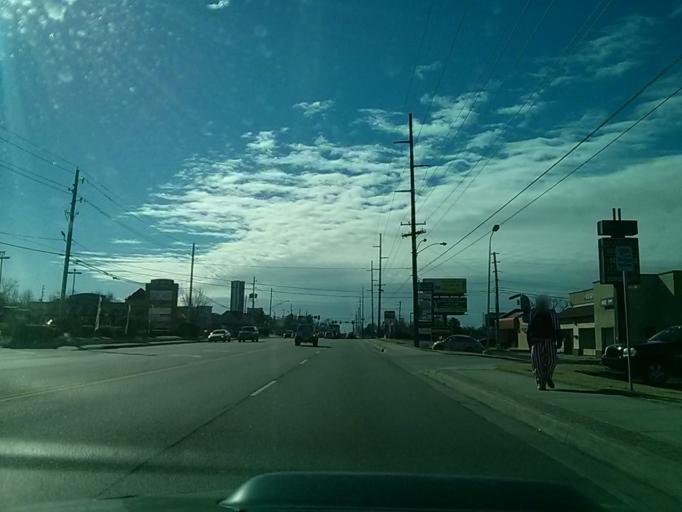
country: US
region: Oklahoma
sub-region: Tulsa County
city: Jenks
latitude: 36.0630
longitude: -95.9580
